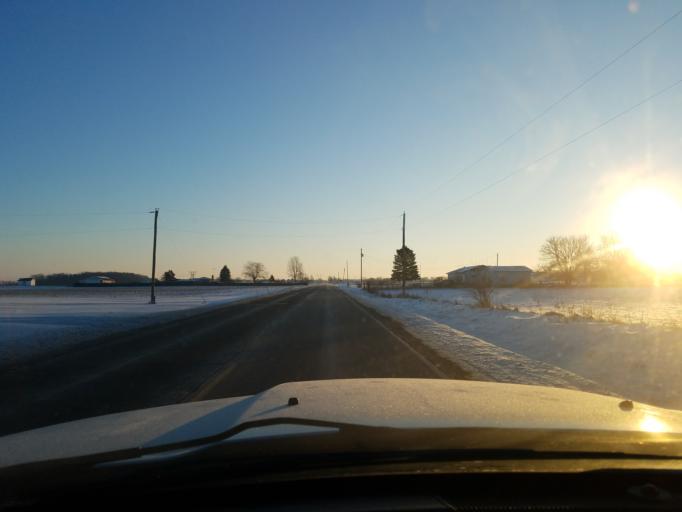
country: US
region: Indiana
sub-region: Marshall County
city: Bremen
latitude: 41.4497
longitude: -86.2586
